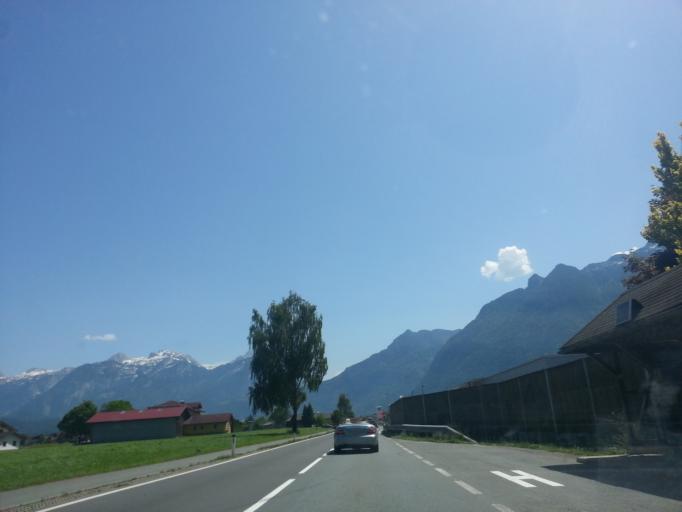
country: AT
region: Salzburg
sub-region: Politischer Bezirk Hallein
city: Kuchl
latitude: 47.6373
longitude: 13.1384
